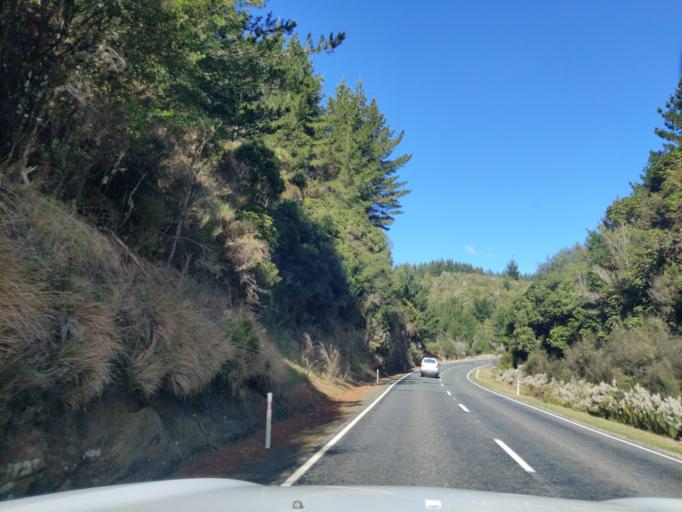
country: NZ
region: Waikato
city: Turangi
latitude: -38.7405
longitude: 175.6834
